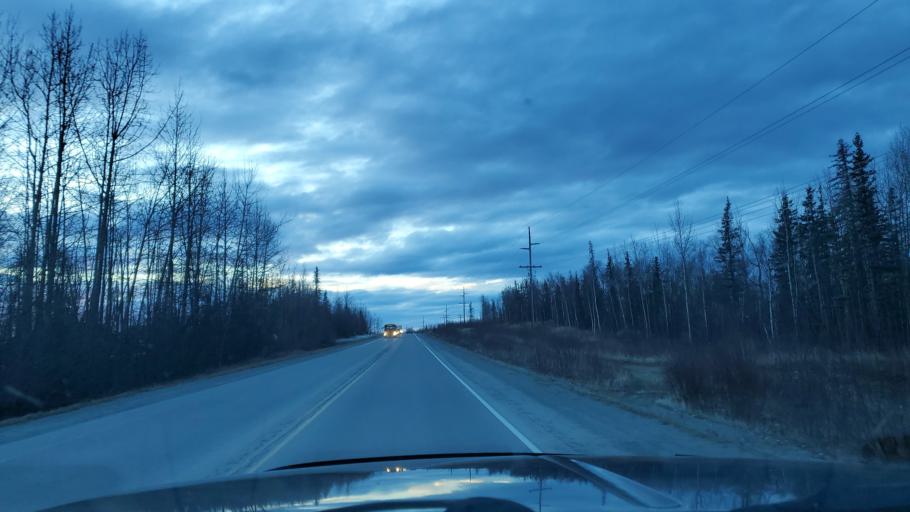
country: US
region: Alaska
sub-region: Matanuska-Susitna Borough
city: Lakes
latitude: 61.5970
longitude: -149.3677
